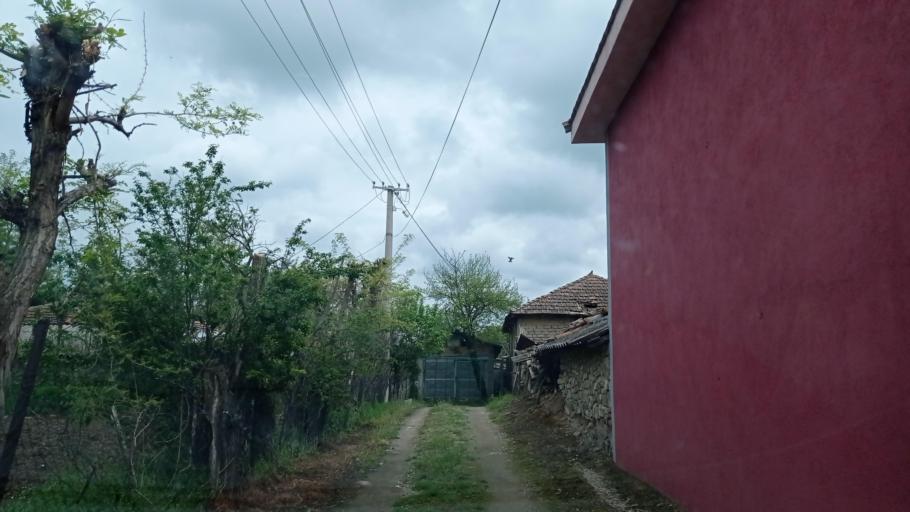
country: MK
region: Lozovo
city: Lozovo
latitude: 41.7636
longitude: 21.8944
